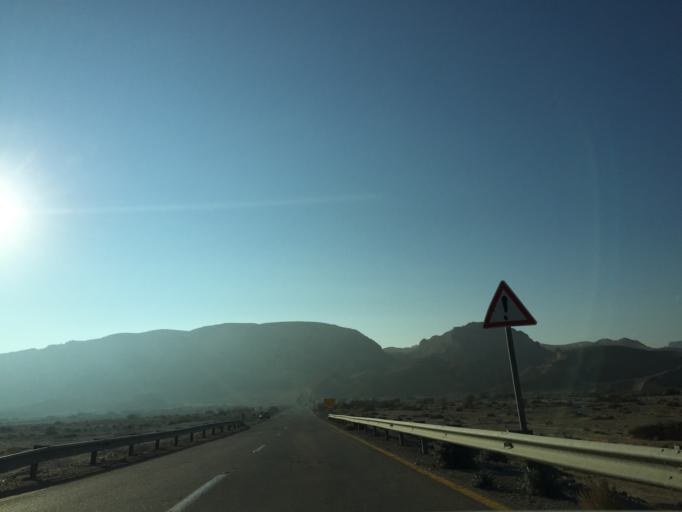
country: IL
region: Southern District
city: Mitzpe Ramon
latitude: 30.3286
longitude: 34.9539
